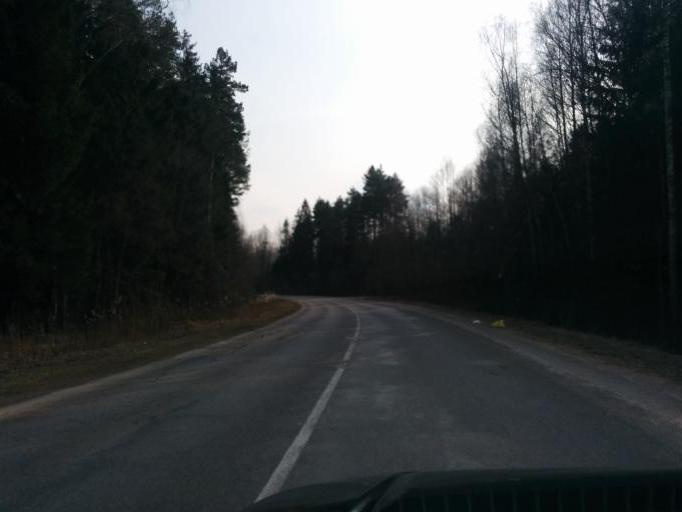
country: LV
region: Kekava
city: Balozi
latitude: 56.7882
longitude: 24.0762
